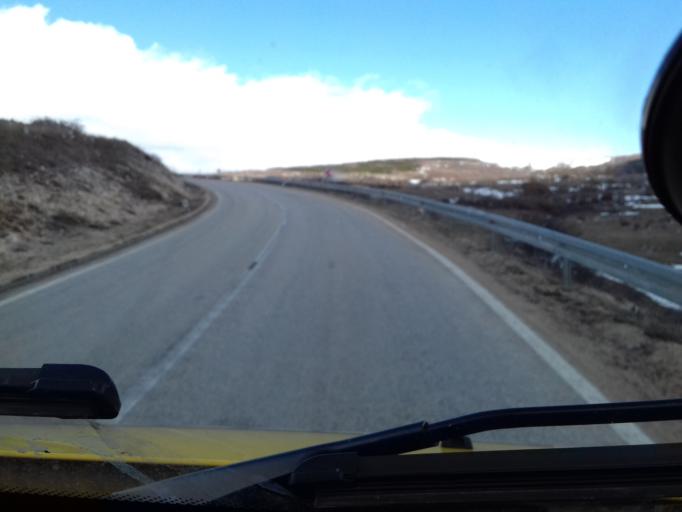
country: BA
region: Federation of Bosnia and Herzegovina
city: Tomislavgrad
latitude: 43.7654
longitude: 17.2379
